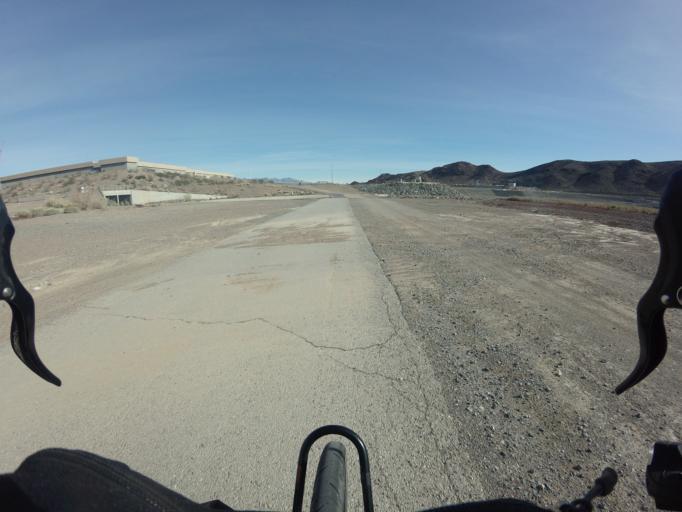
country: US
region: Nevada
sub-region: Clark County
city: Boulder City
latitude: 36.0669
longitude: -114.8107
